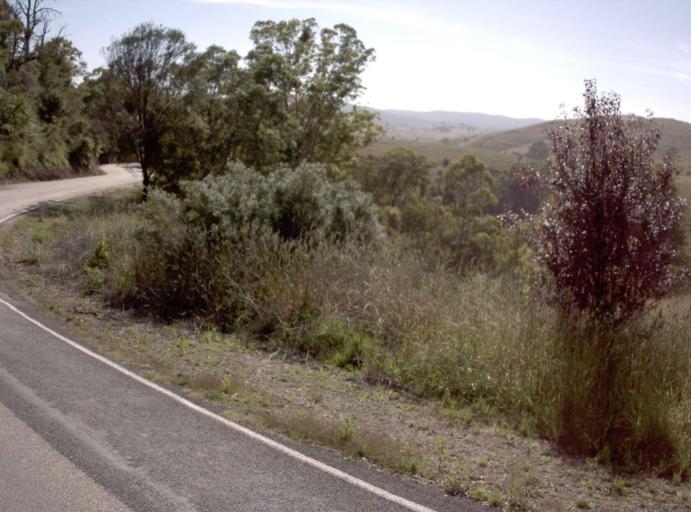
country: AU
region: Victoria
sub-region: East Gippsland
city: Lakes Entrance
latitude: -37.5112
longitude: 148.1683
